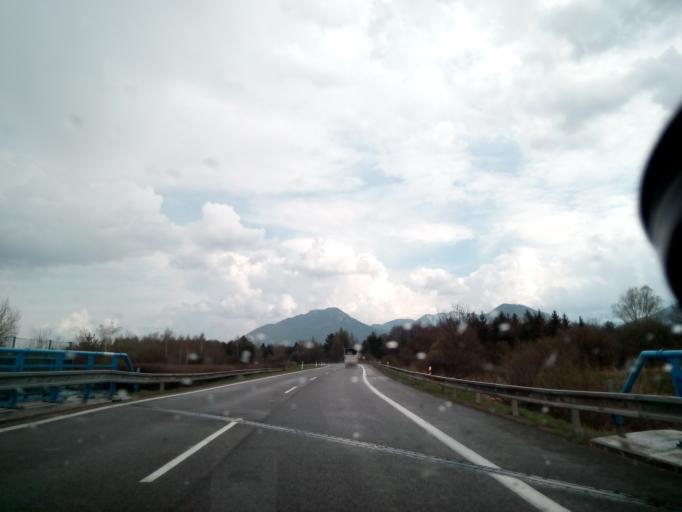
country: SK
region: Zilinsky
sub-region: Okres Liptovsky Mikulas
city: Liptovsky Mikulas
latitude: 49.0858
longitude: 19.5526
